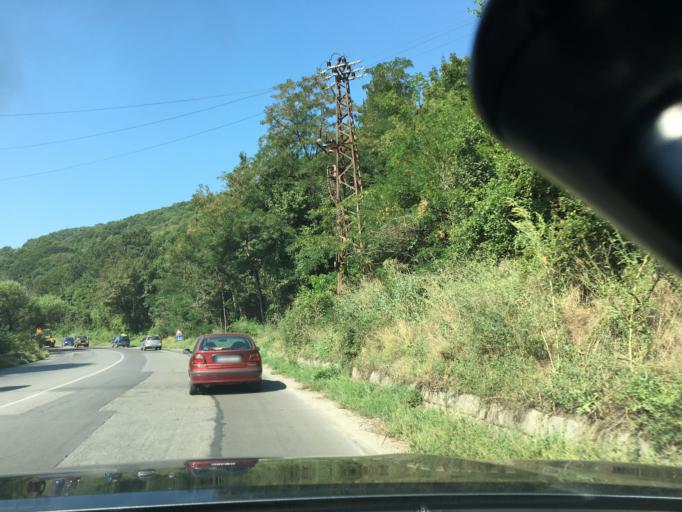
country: BG
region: Sofiya
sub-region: Obshtina Bozhurishte
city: Bozhurishte
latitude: 42.6478
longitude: 23.2101
